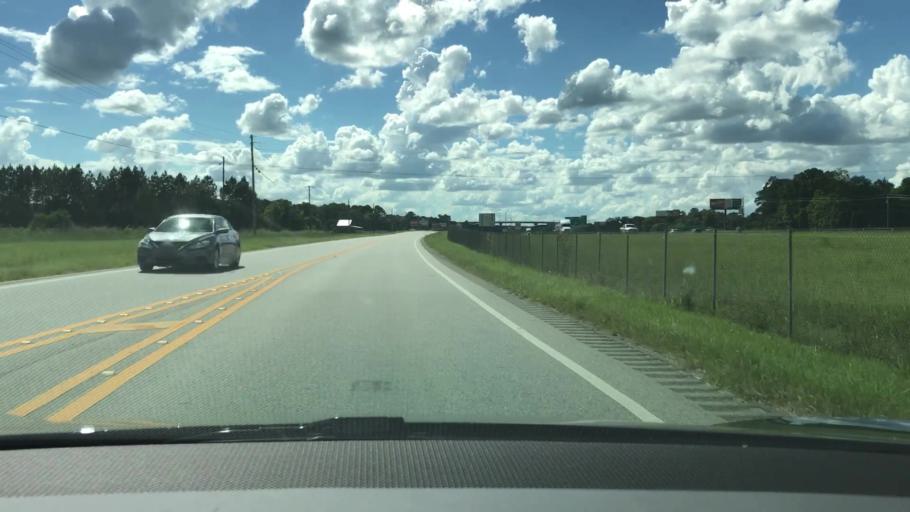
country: US
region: Alabama
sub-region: Montgomery County
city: Pike Road
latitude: 32.3676
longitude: -86.0575
